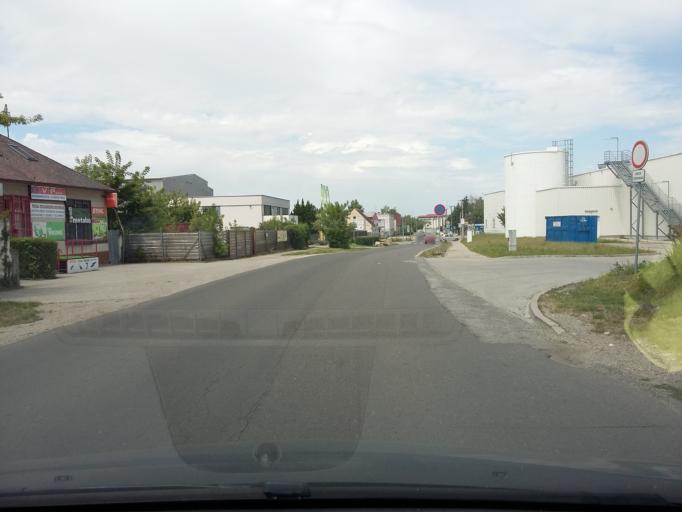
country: SK
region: Bratislavsky
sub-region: Okres Malacky
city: Malacky
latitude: 48.4306
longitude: 17.0295
